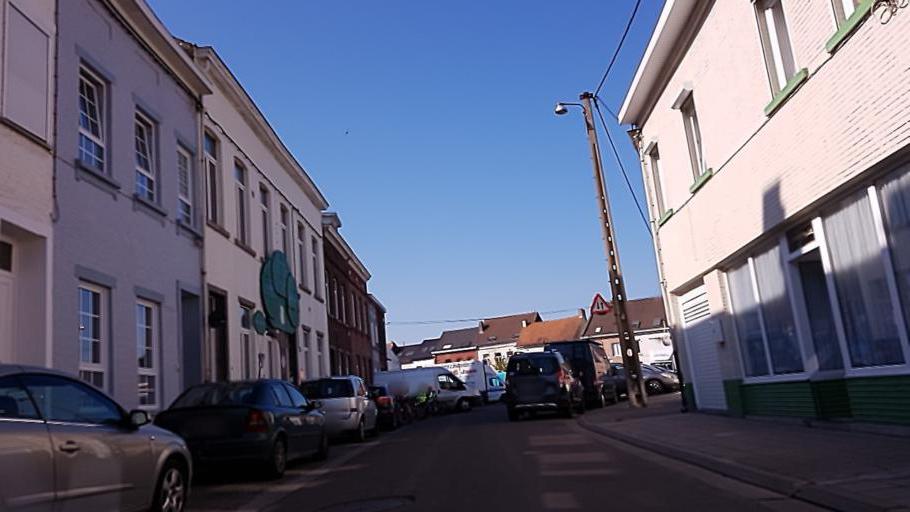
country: BE
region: Wallonia
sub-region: Province du Brabant Wallon
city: Wavre
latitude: 50.7225
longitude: 4.6249
